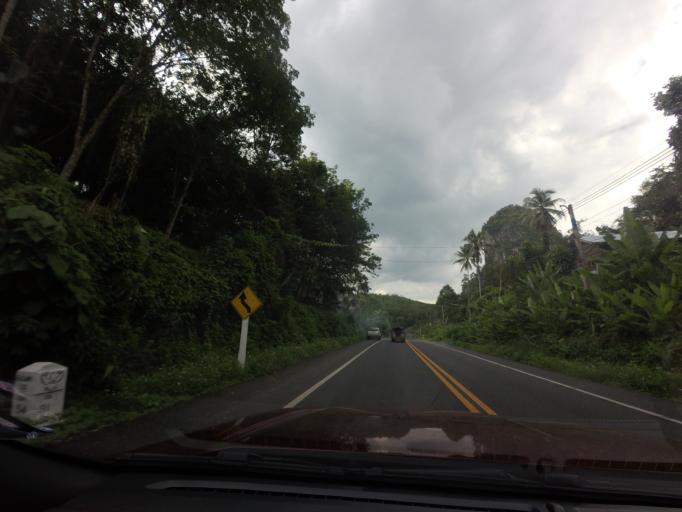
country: TH
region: Yala
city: Than To
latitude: 6.2070
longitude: 101.1691
